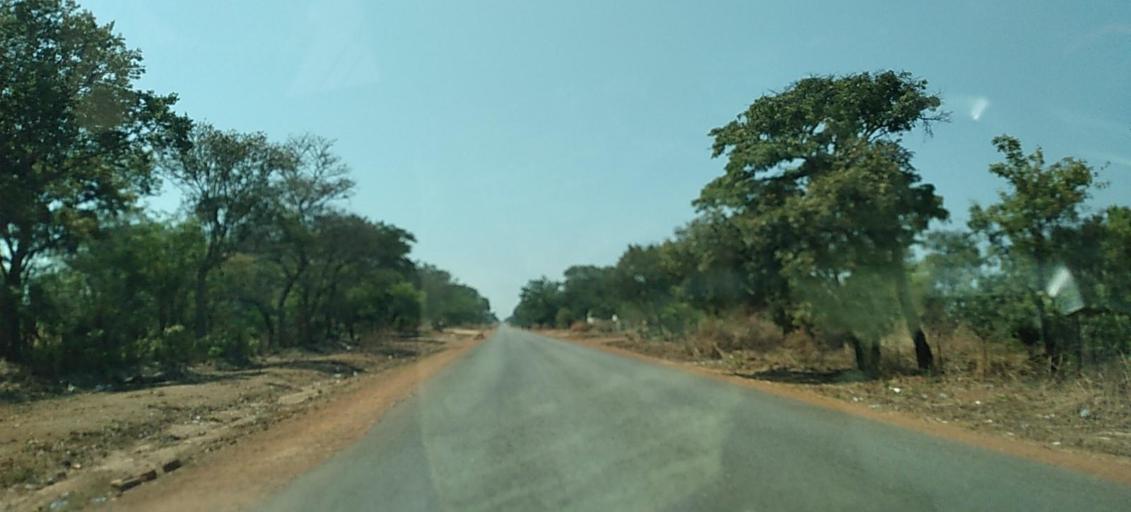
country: ZM
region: North-Western
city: Solwezi
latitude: -12.2785
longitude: 25.6820
